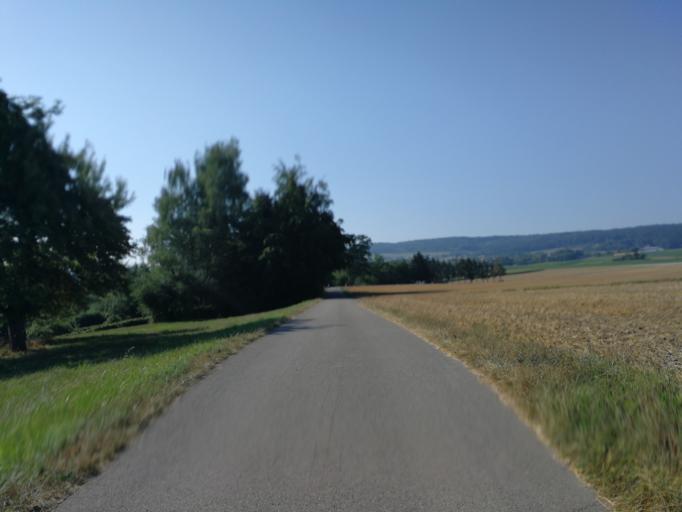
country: CH
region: Thurgau
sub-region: Frauenfeld District
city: Wagenhausen
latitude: 47.6656
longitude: 8.8375
